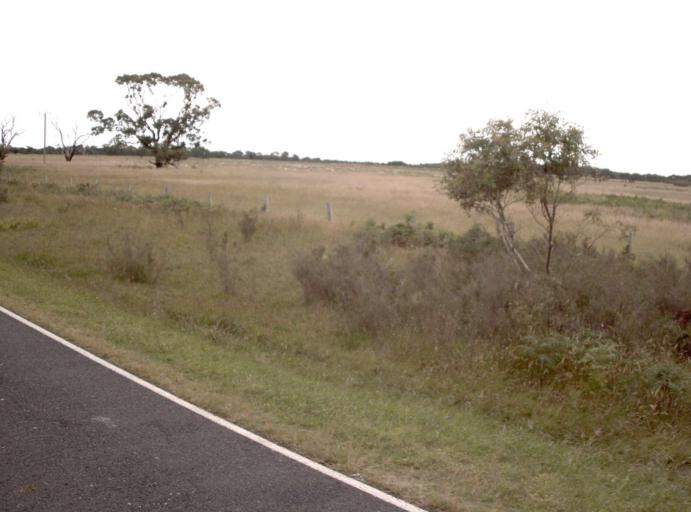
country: AU
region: Victoria
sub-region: Wellington
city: Sale
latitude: -38.5794
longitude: 146.8763
